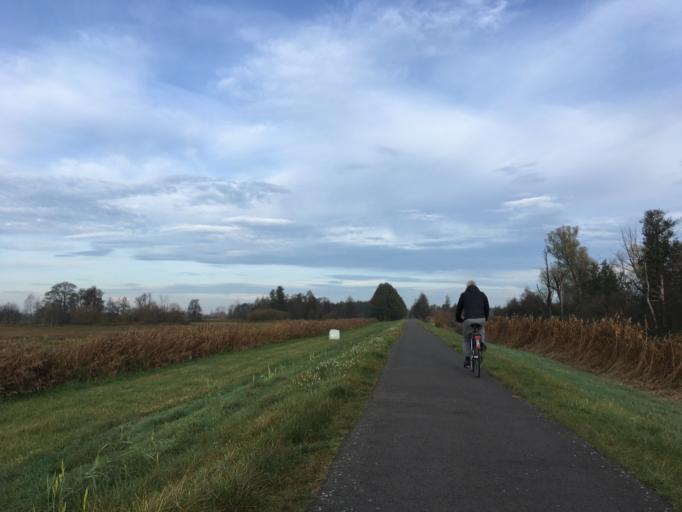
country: DE
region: Brandenburg
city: Luebben
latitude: 51.9114
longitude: 13.9220
